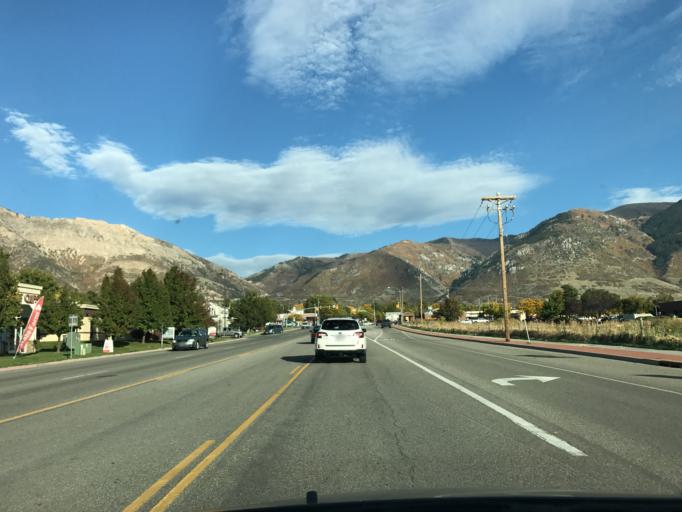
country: US
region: Utah
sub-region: Weber County
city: North Ogden
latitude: 41.3059
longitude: -111.9710
